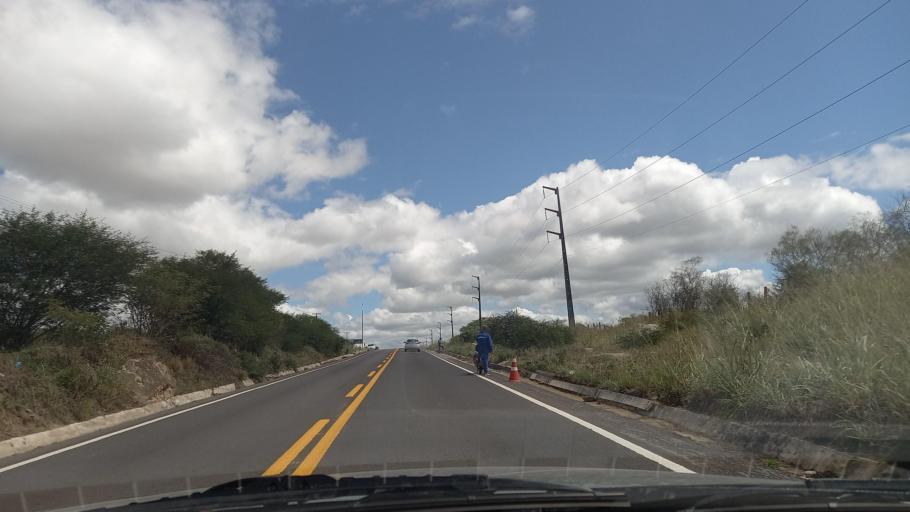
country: BR
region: Pernambuco
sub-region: Caruaru
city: Caruaru
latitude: -8.2562
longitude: -35.9613
